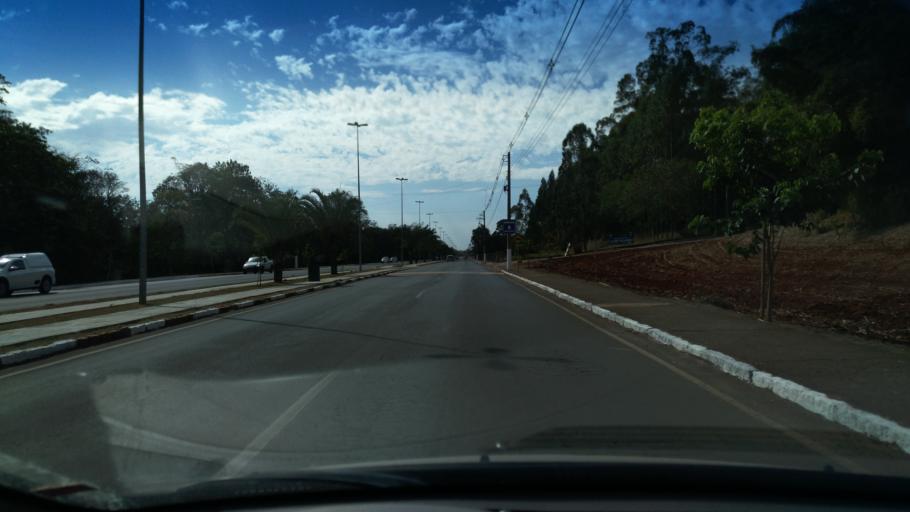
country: BR
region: Sao Paulo
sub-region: Jaguariuna
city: Jaguariuna
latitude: -22.6314
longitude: -47.0612
